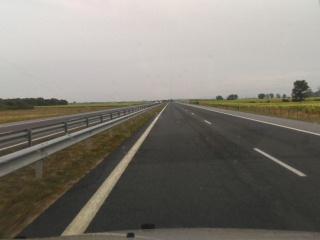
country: BG
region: Stara Zagora
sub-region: Obshtina Radnevo
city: Radnevo
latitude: 42.3765
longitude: 25.8228
